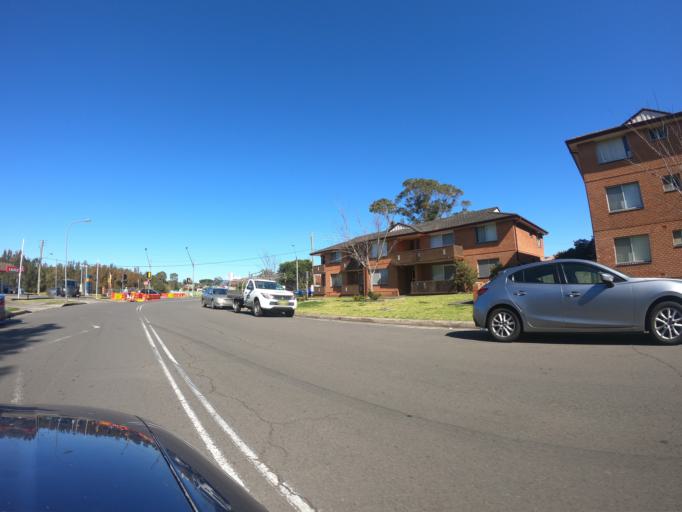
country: AU
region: New South Wales
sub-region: Wollongong
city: Koonawarra
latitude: -34.4853
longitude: 150.8063
